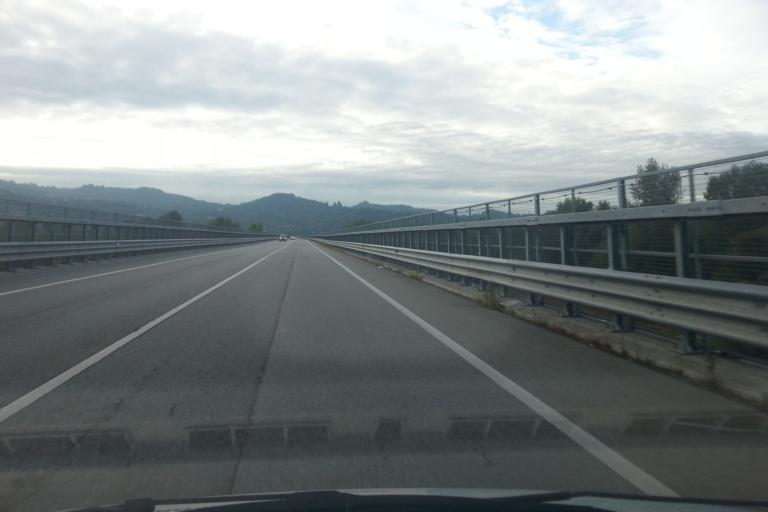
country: IT
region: Piedmont
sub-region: Provincia di Torino
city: Piana San Raffaele
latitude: 45.1567
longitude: 7.8297
